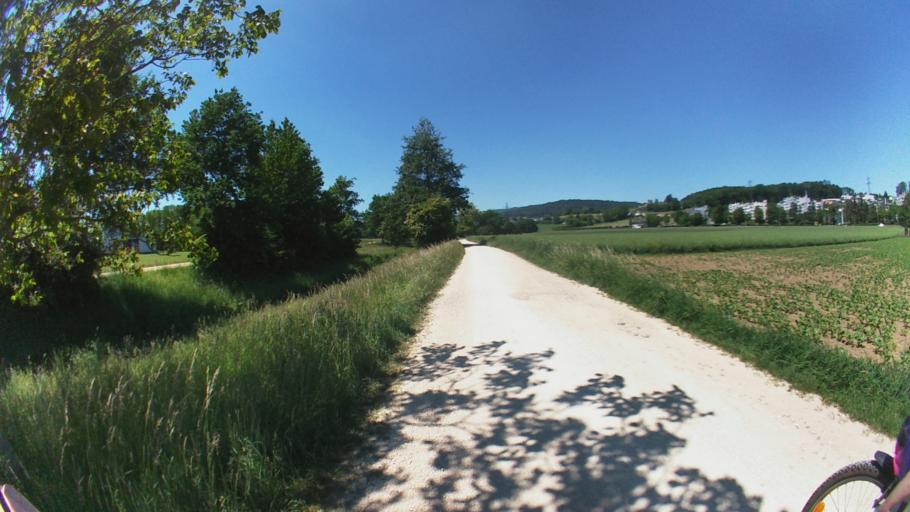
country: CH
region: Zurich
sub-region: Bezirk Dielsdorf
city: Sonnhalde
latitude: 47.4507
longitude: 8.4584
